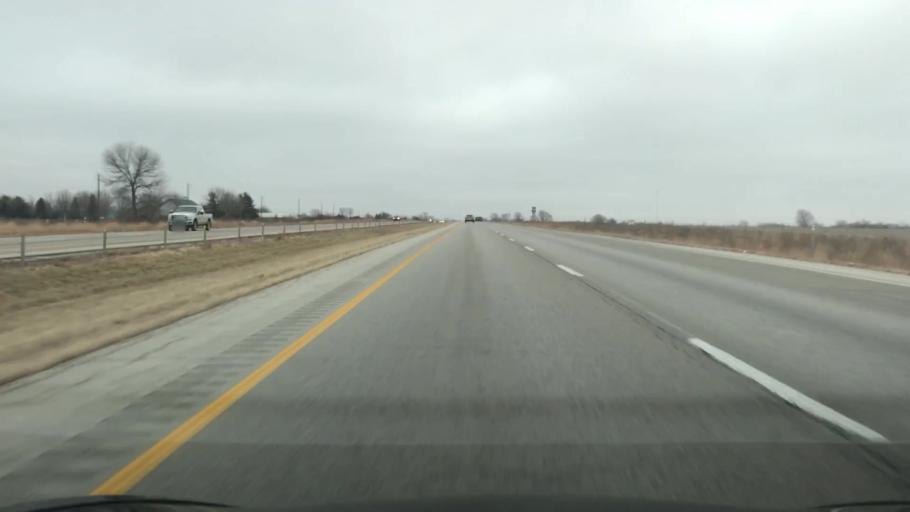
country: US
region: Iowa
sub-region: Madison County
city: Earlham
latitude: 41.5175
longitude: -94.1145
